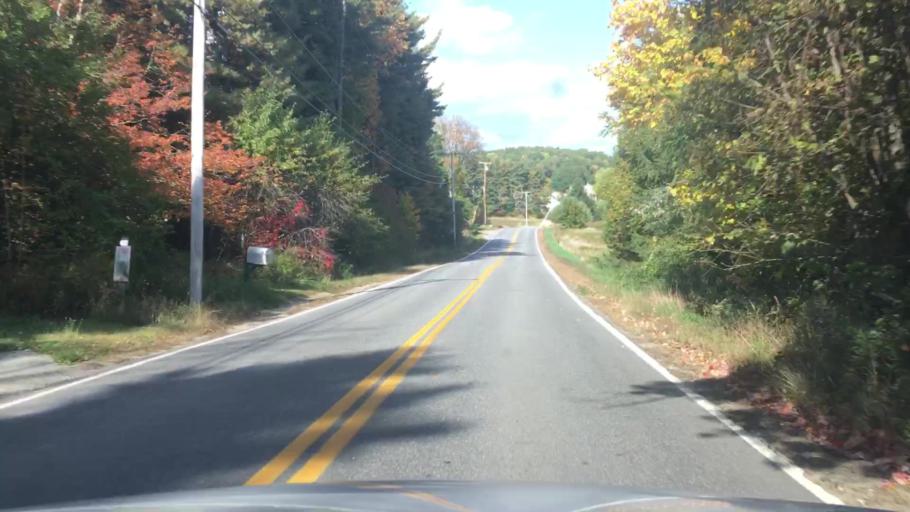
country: US
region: Maine
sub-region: Knox County
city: Union
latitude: 44.2263
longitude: -69.2840
